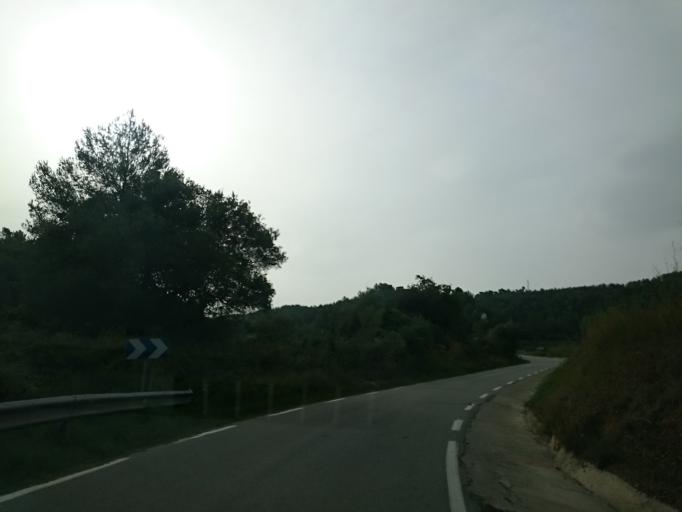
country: ES
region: Catalonia
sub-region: Provincia de Barcelona
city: Olivella
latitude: 41.3126
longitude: 1.8069
